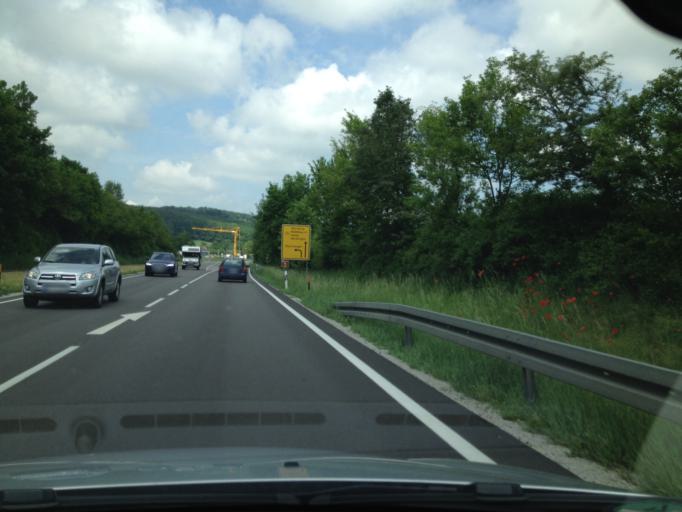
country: DE
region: Bavaria
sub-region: Swabia
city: Harburg
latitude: 48.7596
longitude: 10.7144
